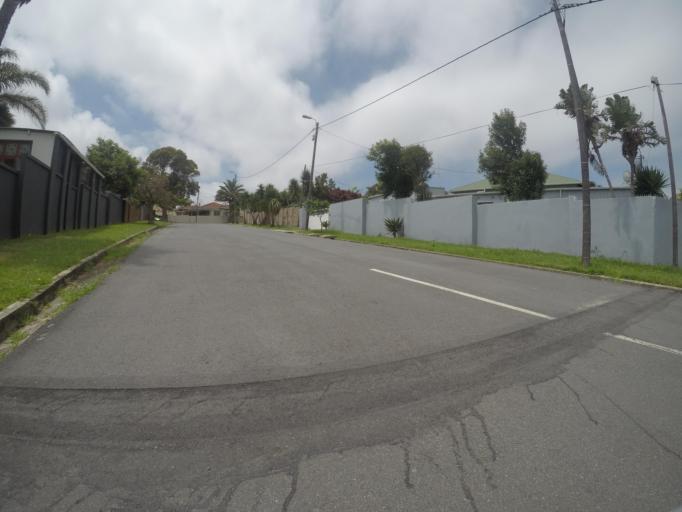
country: ZA
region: Eastern Cape
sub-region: Buffalo City Metropolitan Municipality
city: East London
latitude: -32.9950
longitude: 27.9099
